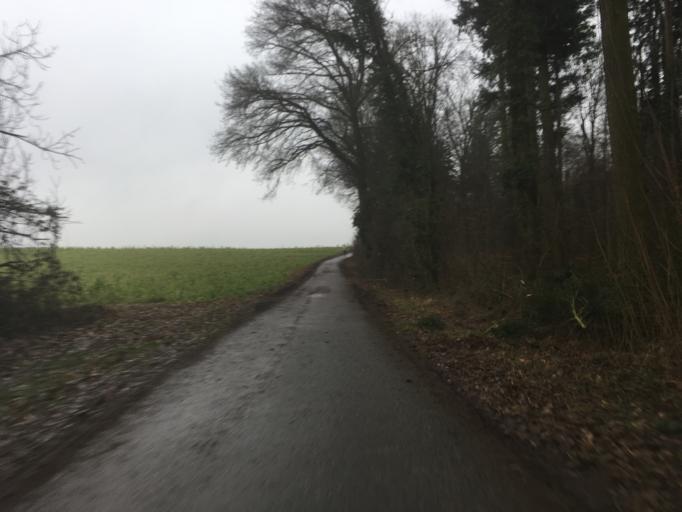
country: DE
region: Baden-Wuerttemberg
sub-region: Karlsruhe Region
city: Ettlingen
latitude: 48.9763
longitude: 8.4772
